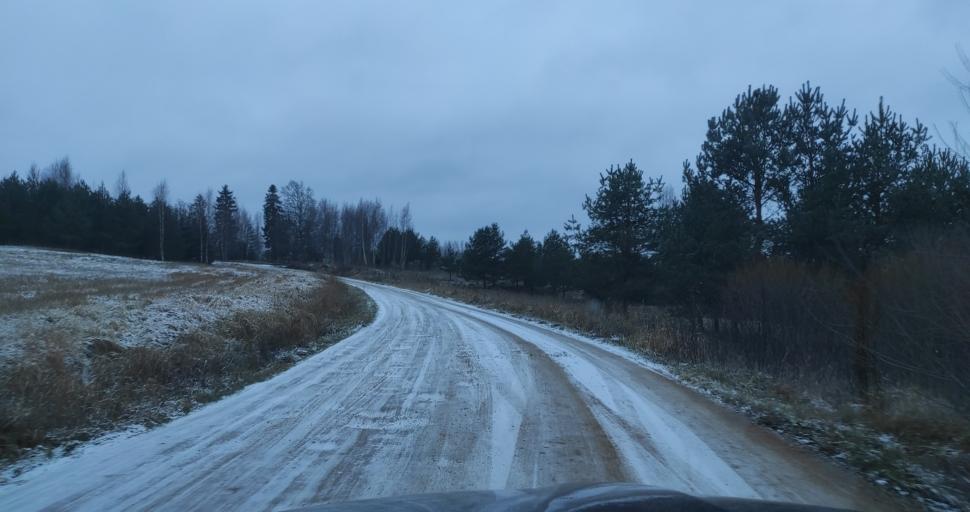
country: LV
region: Kuldigas Rajons
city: Kuldiga
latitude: 56.9814
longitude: 22.0511
